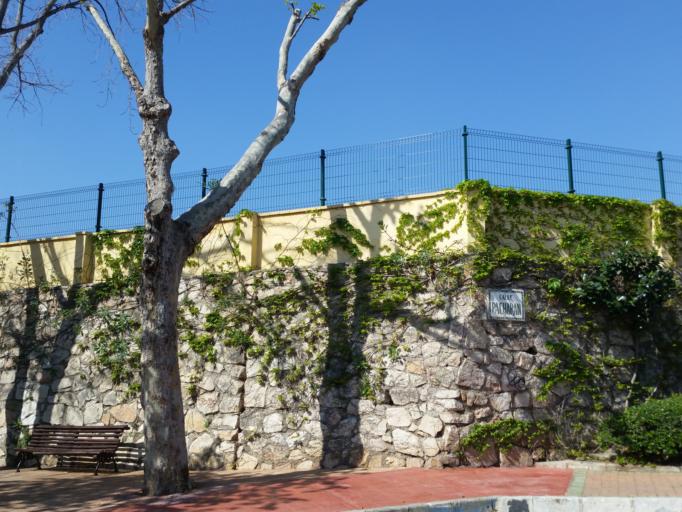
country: ES
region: Andalusia
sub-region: Provincia de Malaga
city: Torremolinos
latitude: 36.6040
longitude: -4.5310
